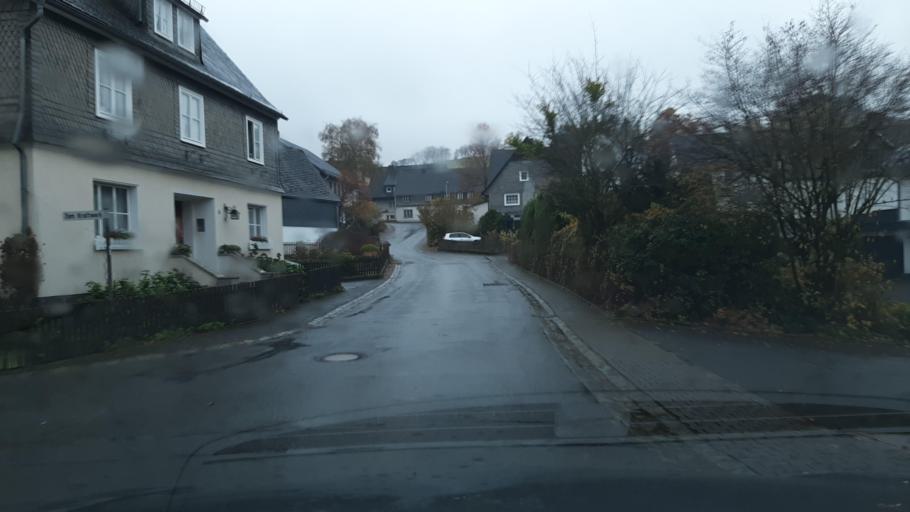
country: DE
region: North Rhine-Westphalia
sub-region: Regierungsbezirk Arnsberg
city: Olsberg
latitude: 51.2903
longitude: 8.5032
